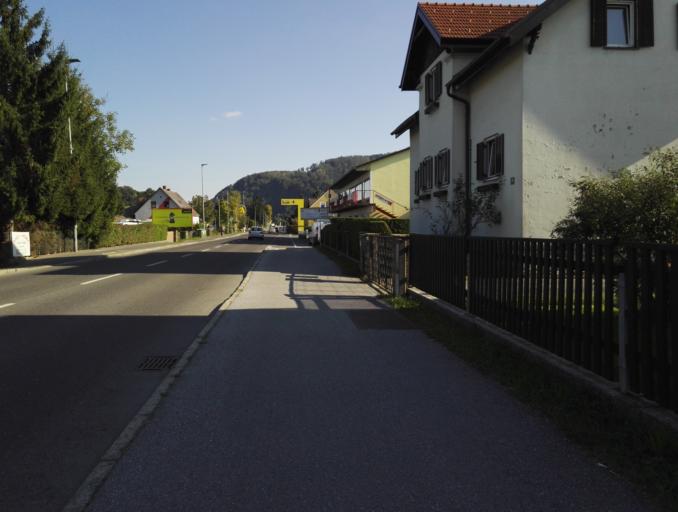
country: AT
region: Styria
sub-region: Politischer Bezirk Graz-Umgebung
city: Gratkorn
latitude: 47.1286
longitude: 15.3447
